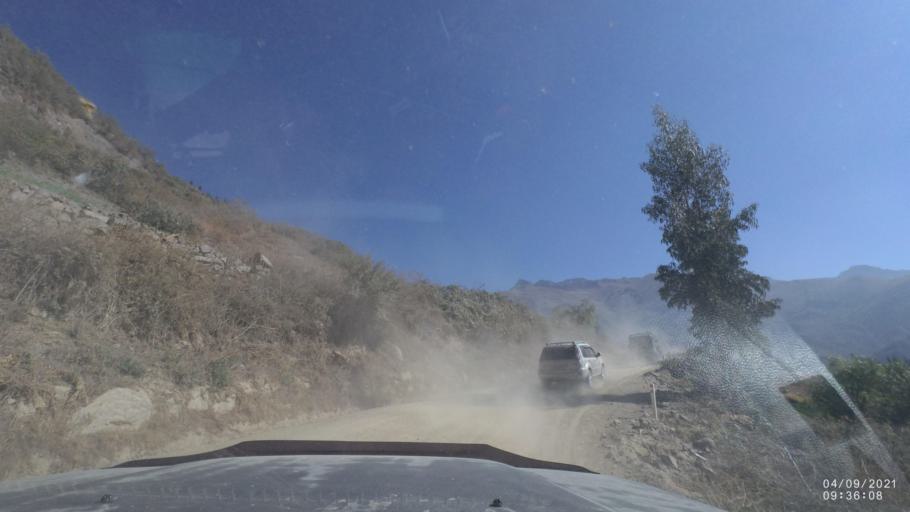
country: BO
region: Cochabamba
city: Sipe Sipe
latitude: -17.3517
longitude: -66.3819
